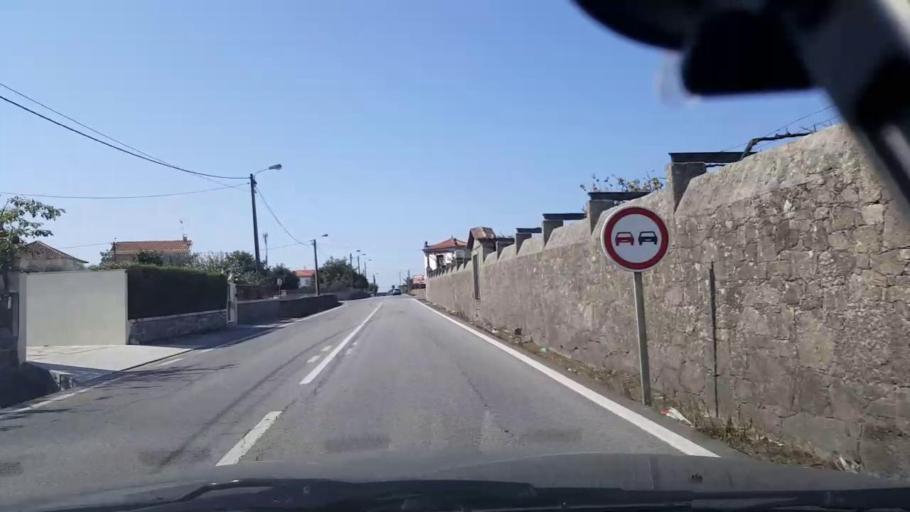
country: PT
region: Porto
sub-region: Vila do Conde
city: Vila do Conde
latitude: 41.3834
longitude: -8.7248
